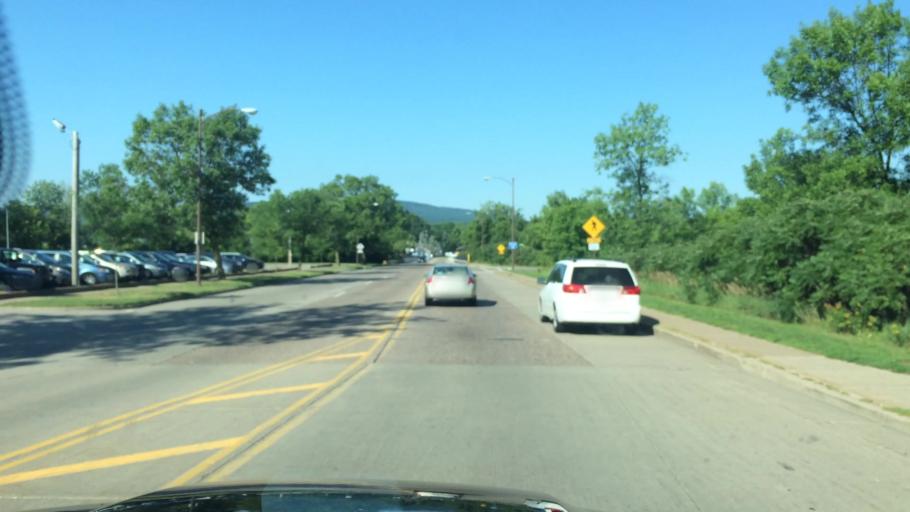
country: US
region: Wisconsin
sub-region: Marathon County
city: Wausau
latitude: 44.9506
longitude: -89.6248
